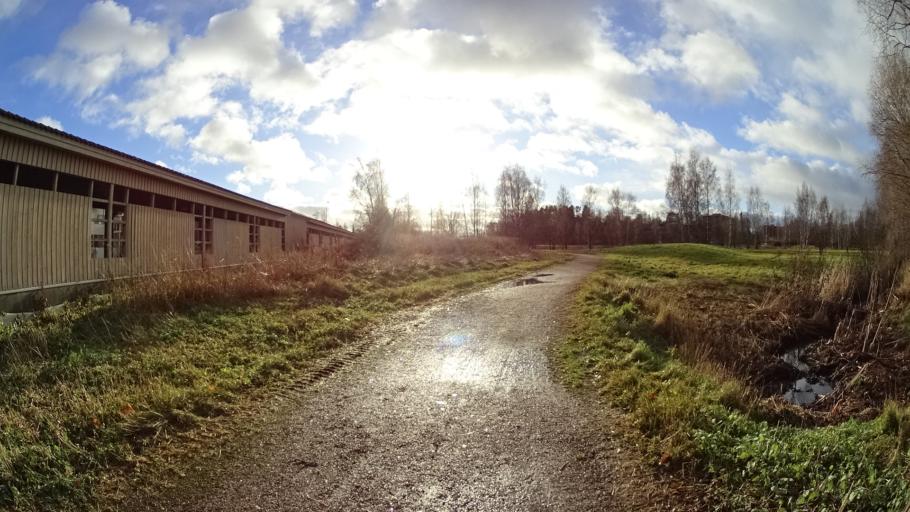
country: FI
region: Uusimaa
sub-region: Helsinki
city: Kilo
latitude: 60.1843
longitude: 24.7806
